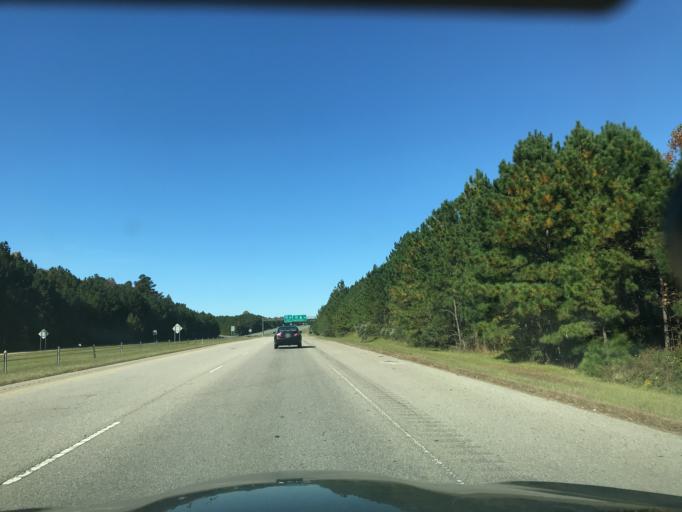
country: US
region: North Carolina
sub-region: Wake County
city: Morrisville
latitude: 35.8831
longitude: -78.8098
